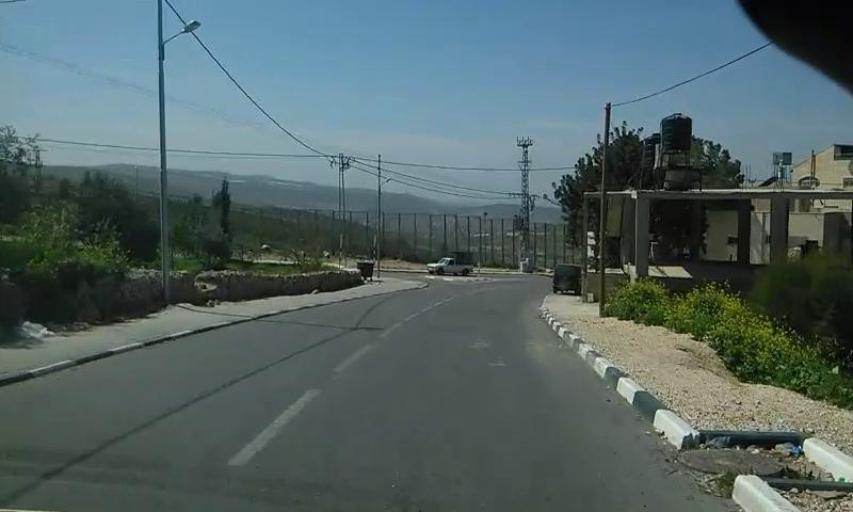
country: PS
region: West Bank
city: Husan
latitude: 31.7069
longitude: 35.1399
